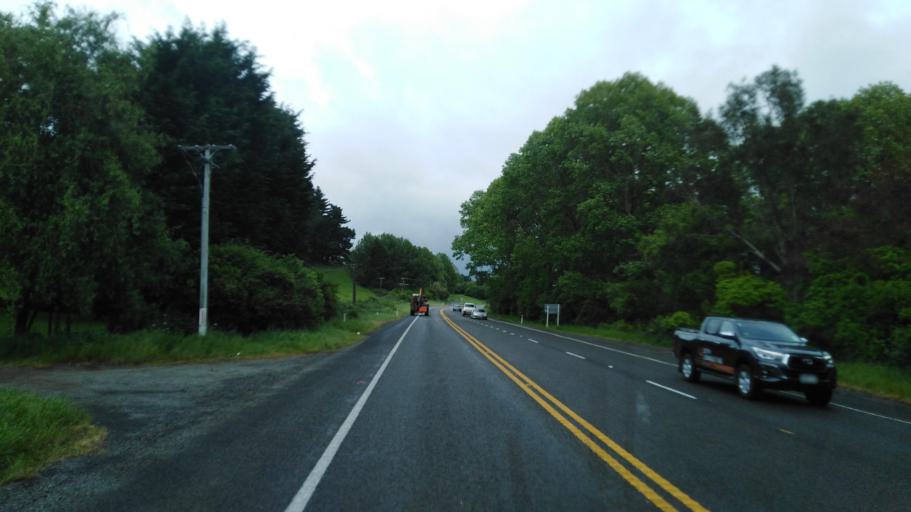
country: NZ
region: Wellington
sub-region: Kapiti Coast District
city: Otaki
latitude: -40.7391
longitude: 175.1826
